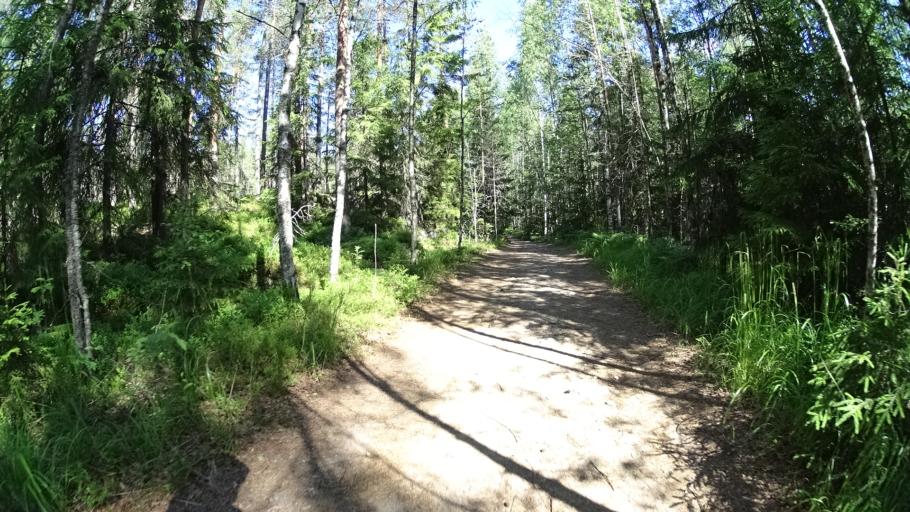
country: FI
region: Uusimaa
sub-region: Helsinki
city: Espoo
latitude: 60.3209
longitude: 24.4942
